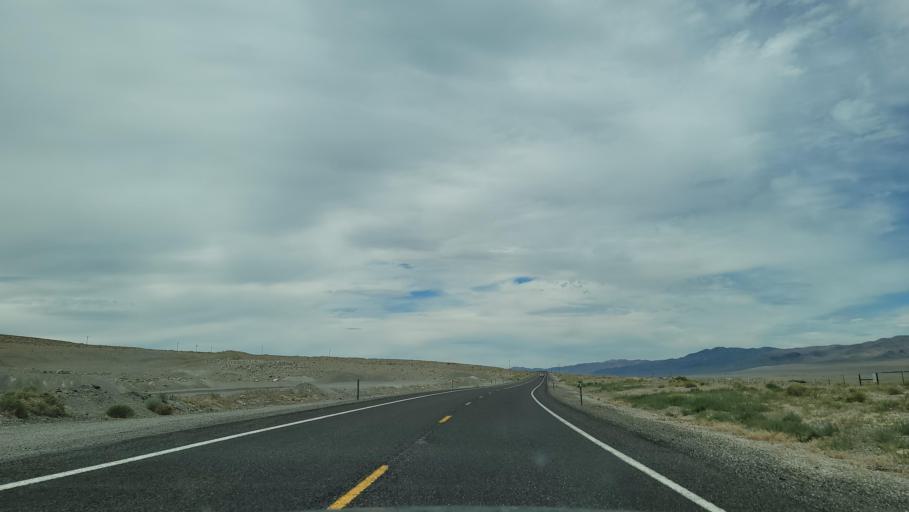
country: US
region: Nevada
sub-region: Mineral County
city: Hawthorne
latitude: 38.5879
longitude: -118.7091
